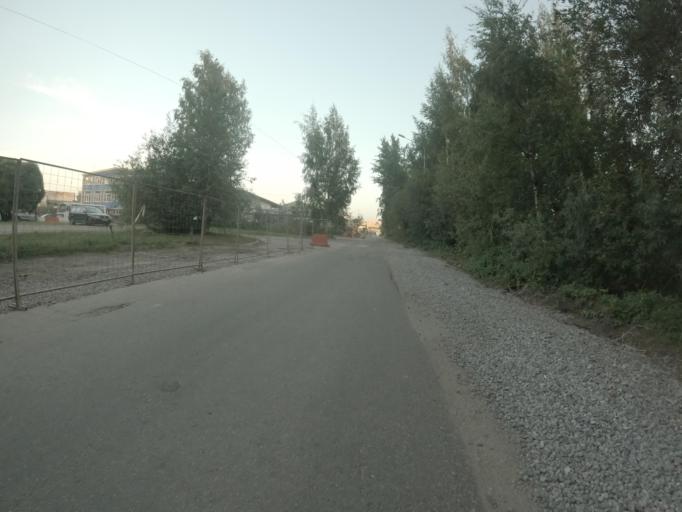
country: RU
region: St.-Petersburg
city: Krasnogvargeisky
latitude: 59.9457
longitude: 30.4481
